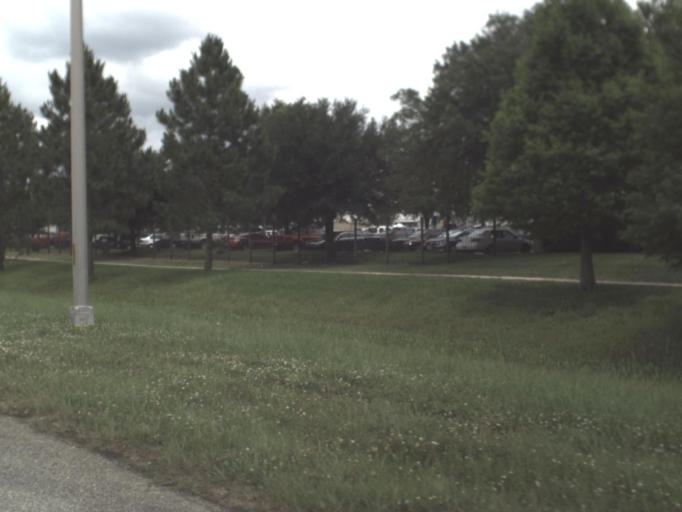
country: US
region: Florida
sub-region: Duval County
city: Jacksonville
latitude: 30.4761
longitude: -81.6642
